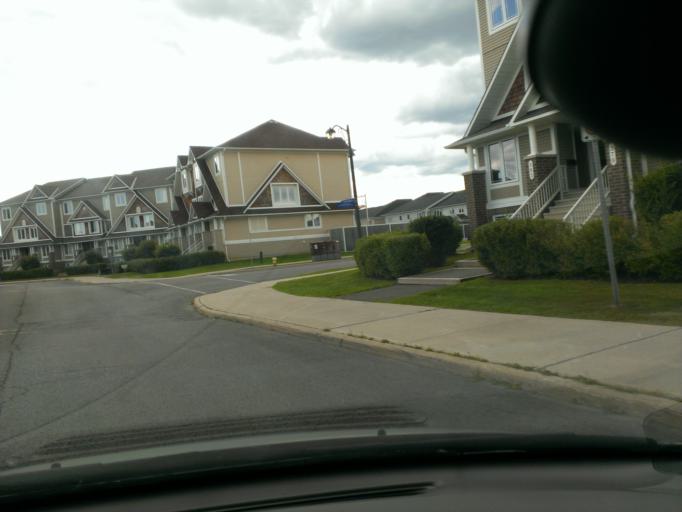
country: CA
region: Ontario
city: Clarence-Rockland
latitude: 45.4494
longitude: -75.4766
